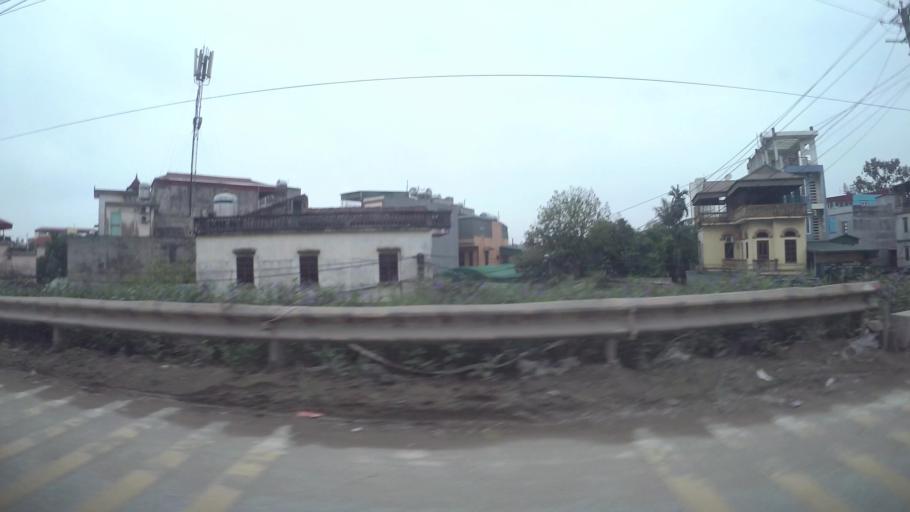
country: VN
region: Ha Noi
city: Hai BaTrung
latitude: 20.9922
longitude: 105.8921
